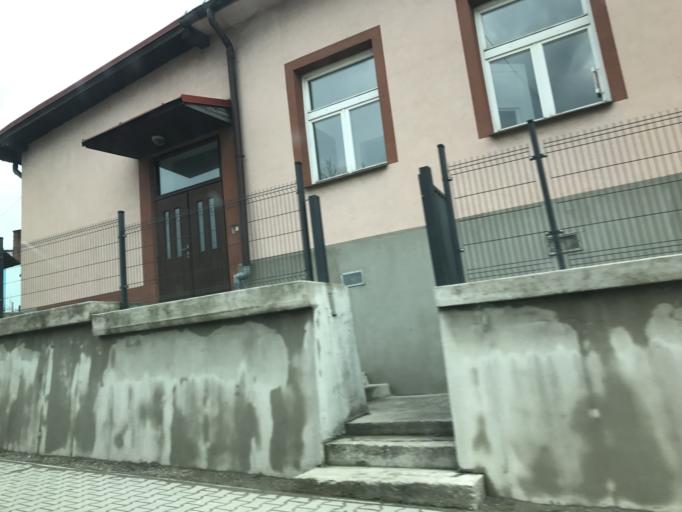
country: SK
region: Zilinsky
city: Namestovo
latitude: 49.4480
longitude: 19.5104
